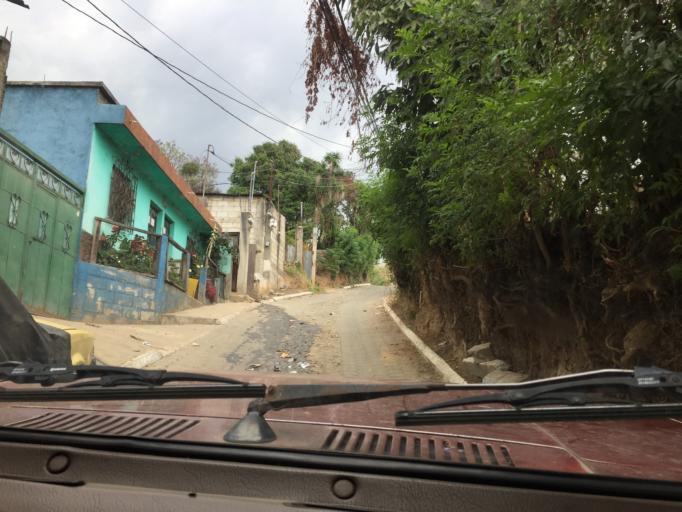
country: GT
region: Guatemala
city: Amatitlan
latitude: 14.4949
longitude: -90.6433
